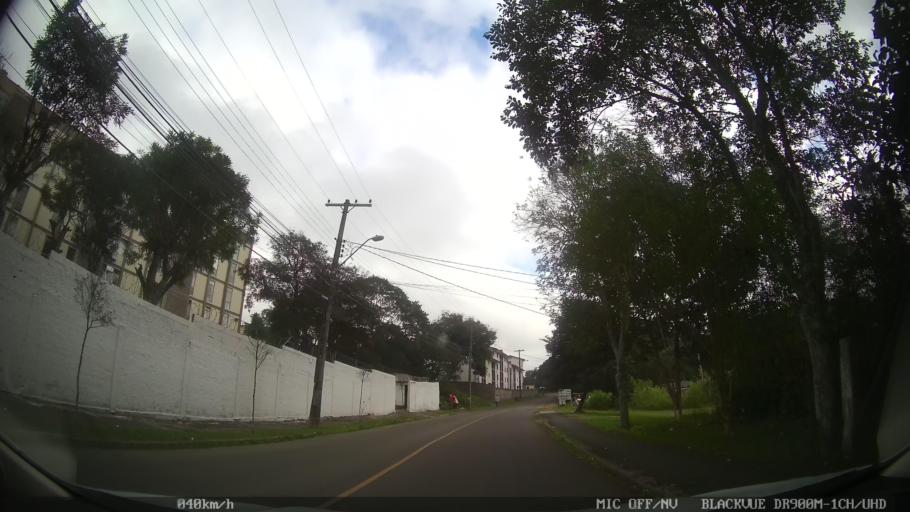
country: BR
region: Parana
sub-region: Curitiba
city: Curitiba
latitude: -25.3751
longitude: -49.2587
